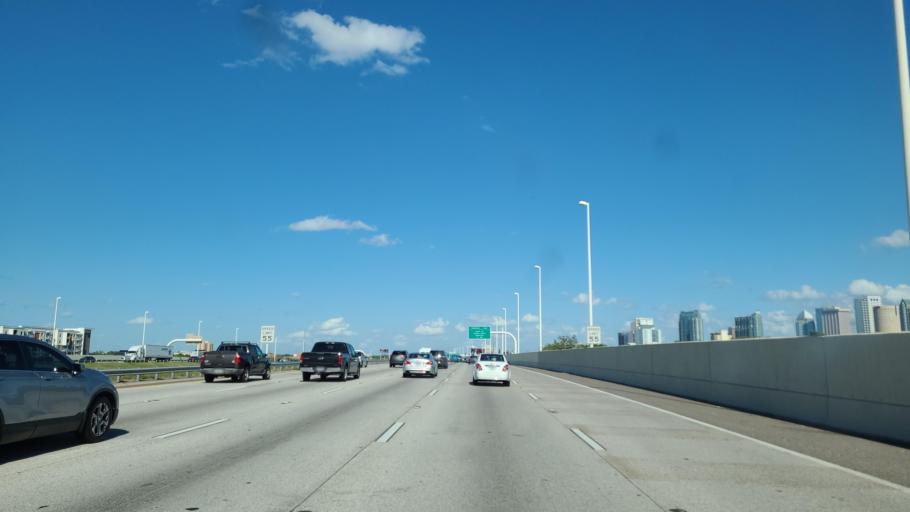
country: US
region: Florida
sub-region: Hillsborough County
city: Tampa
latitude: 27.9543
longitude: -82.4747
